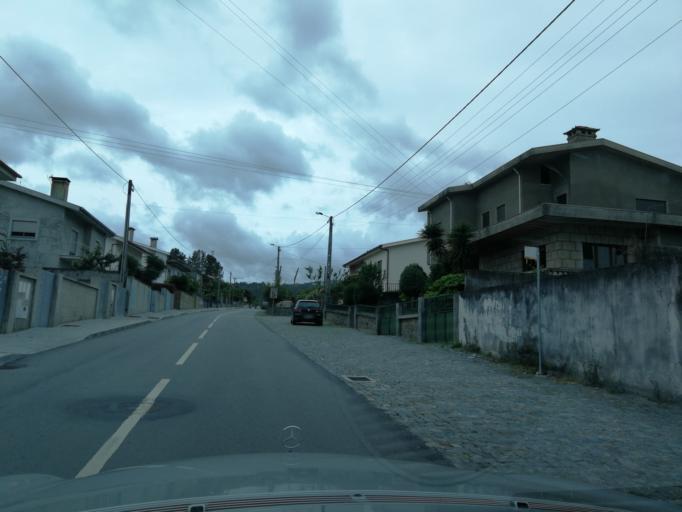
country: PT
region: Braga
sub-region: Braga
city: Adaufe
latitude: 41.6049
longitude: -8.3822
